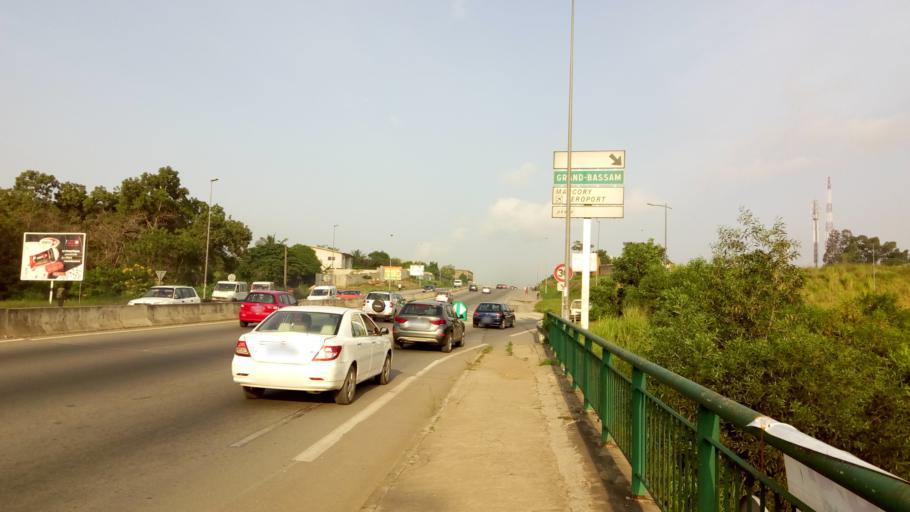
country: CI
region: Lagunes
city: Abidjan
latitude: 5.3519
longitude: -3.9834
